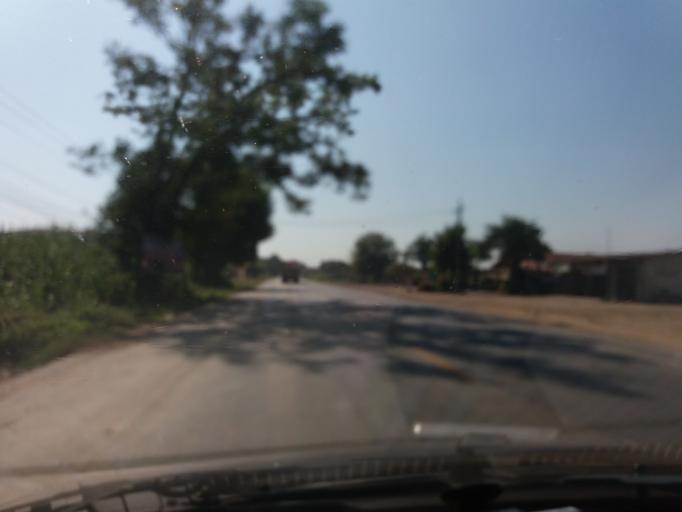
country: TH
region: Kamphaeng Phet
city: Khlong Khlung
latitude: 16.1607
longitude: 99.8036
